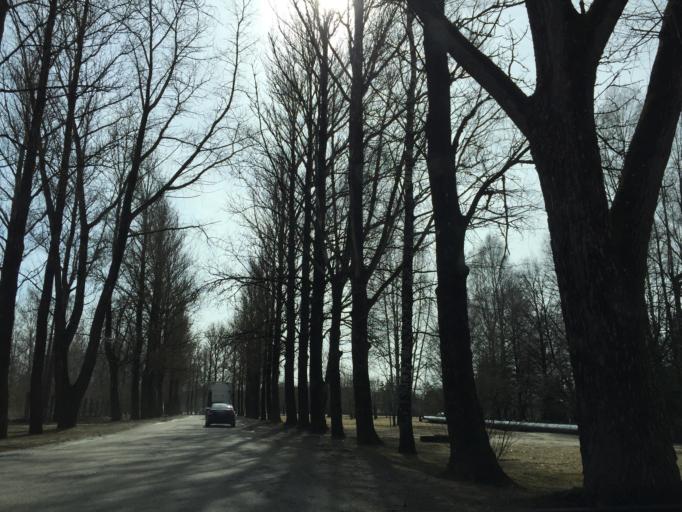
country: EE
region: Paernumaa
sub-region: Paernu linn
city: Parnu
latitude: 58.3764
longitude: 24.5405
